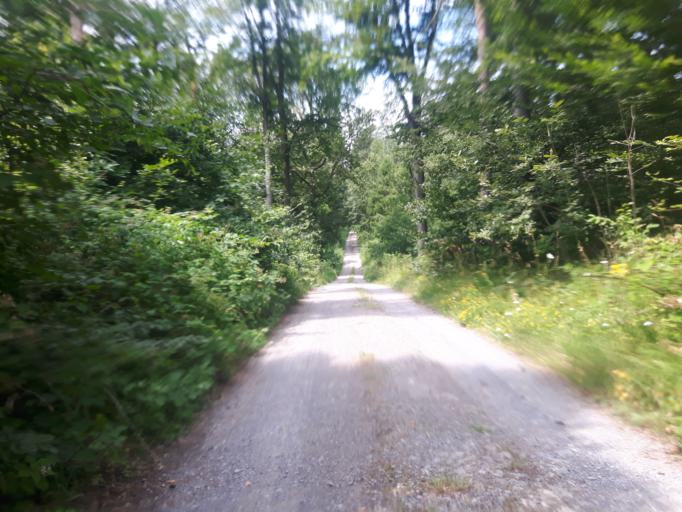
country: DE
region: Baden-Wuerttemberg
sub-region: Regierungsbezirk Stuttgart
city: Cleebronn
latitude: 49.0288
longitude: 9.0283
